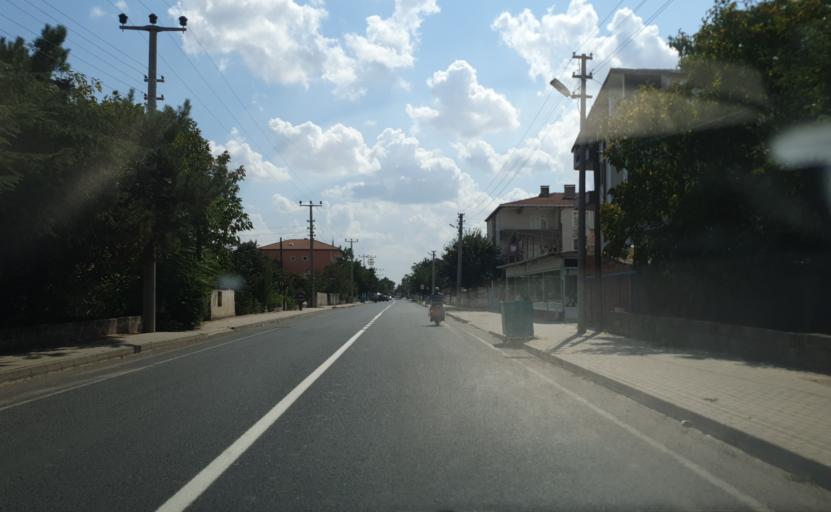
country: TR
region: Kirklareli
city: Luleburgaz
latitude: 41.3613
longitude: 27.3366
